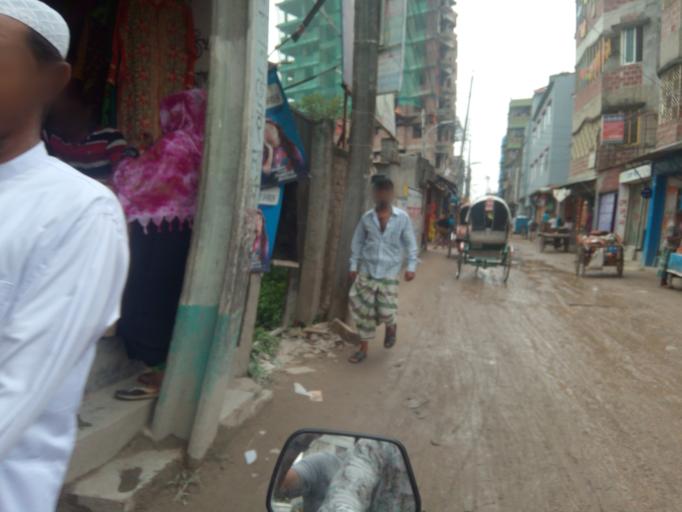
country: BD
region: Dhaka
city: Paltan
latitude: 23.7549
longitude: 90.4303
